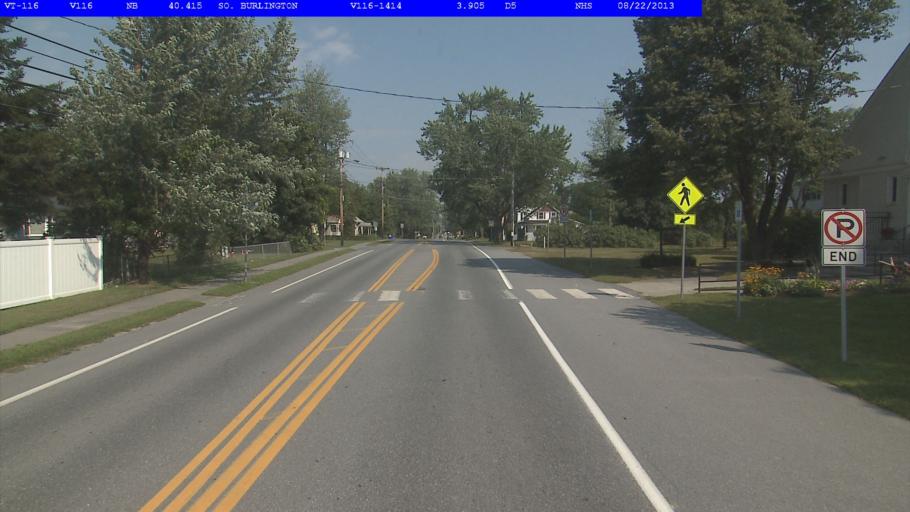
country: US
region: Vermont
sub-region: Chittenden County
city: South Burlington
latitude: 44.4622
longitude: -73.1704
